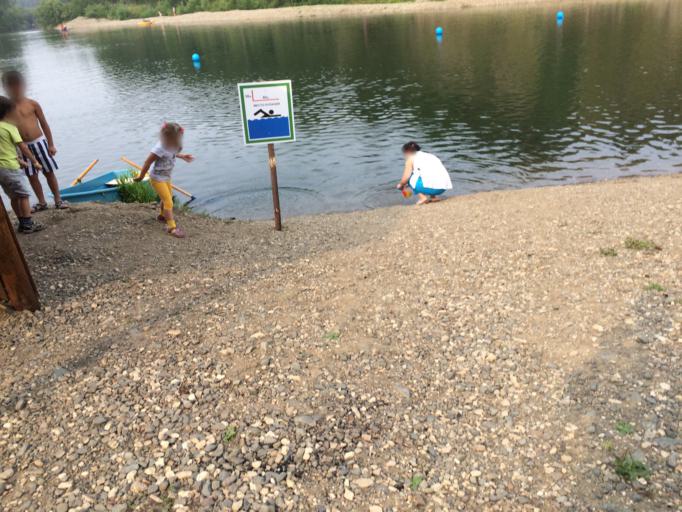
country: RU
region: Bashkortostan
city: Abzakovo
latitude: 53.7966
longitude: 58.6296
